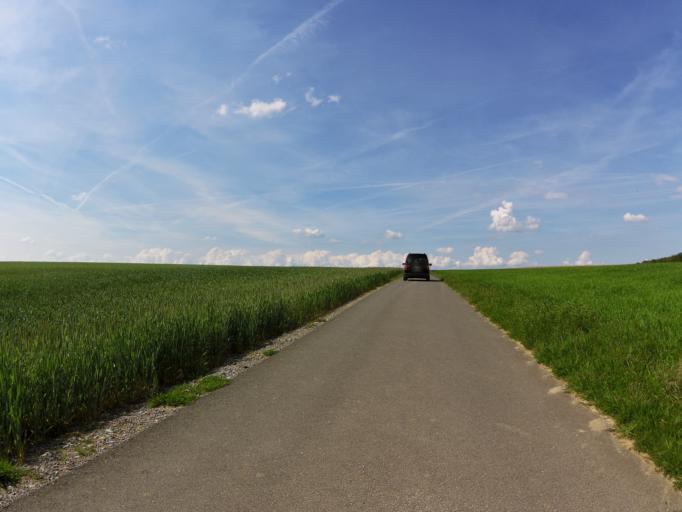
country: DE
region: Bavaria
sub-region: Regierungsbezirk Unterfranken
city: Theilheim
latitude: 49.7367
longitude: 10.0249
